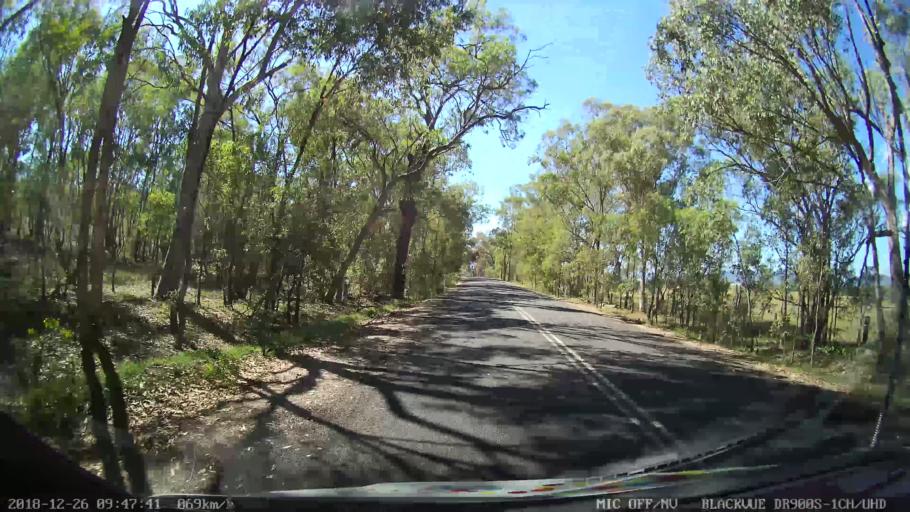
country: AU
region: New South Wales
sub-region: Mid-Western Regional
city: Kandos
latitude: -32.9815
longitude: 150.1077
